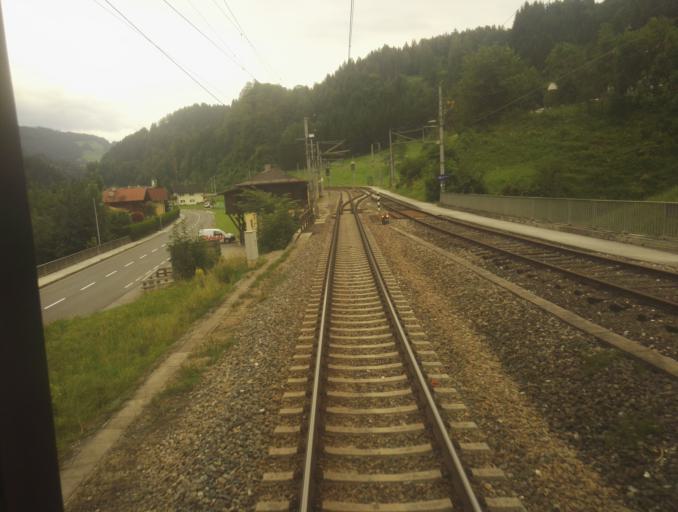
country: AT
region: Salzburg
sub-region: Politischer Bezirk Sankt Johann im Pongau
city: Werfenweng
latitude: 47.4310
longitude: 13.2532
